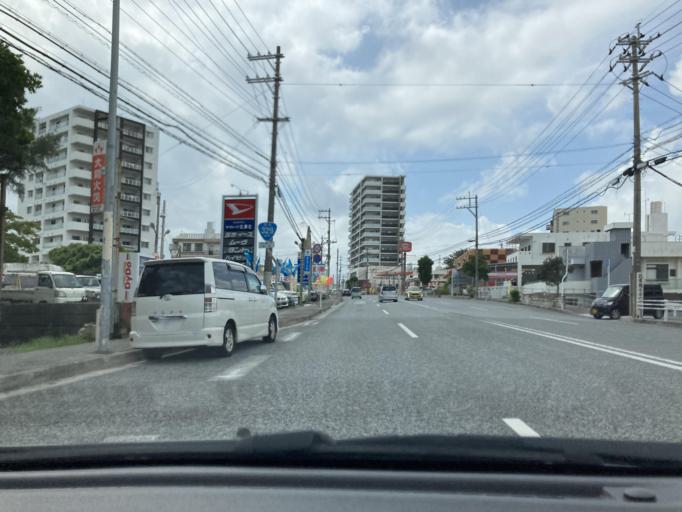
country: JP
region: Okinawa
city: Okinawa
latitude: 26.3126
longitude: 127.8173
